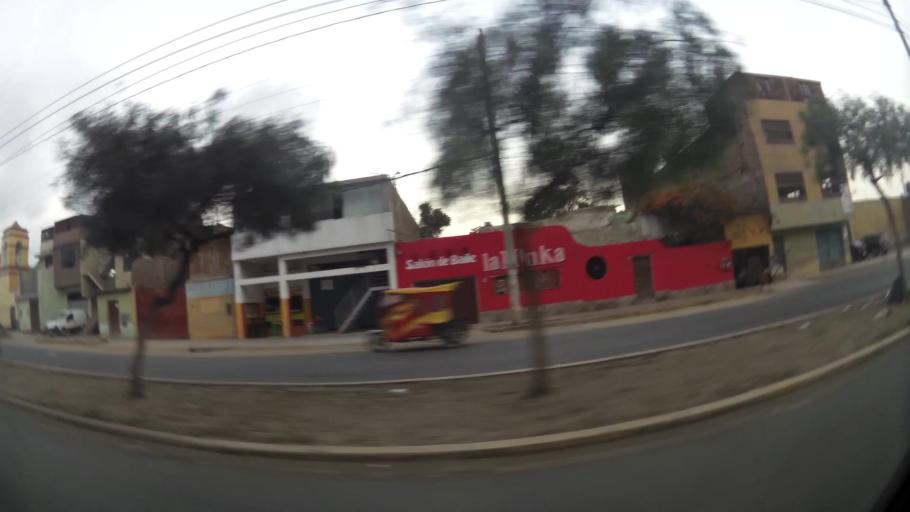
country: PE
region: La Libertad
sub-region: Provincia de Trujillo
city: El Porvenir
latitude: -8.0889
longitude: -79.0162
